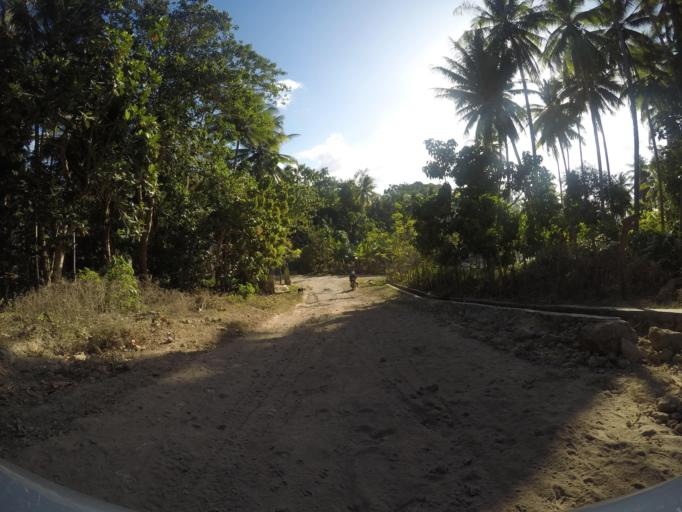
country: TL
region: Lautem
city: Lospalos
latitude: -8.4395
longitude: 126.8558
